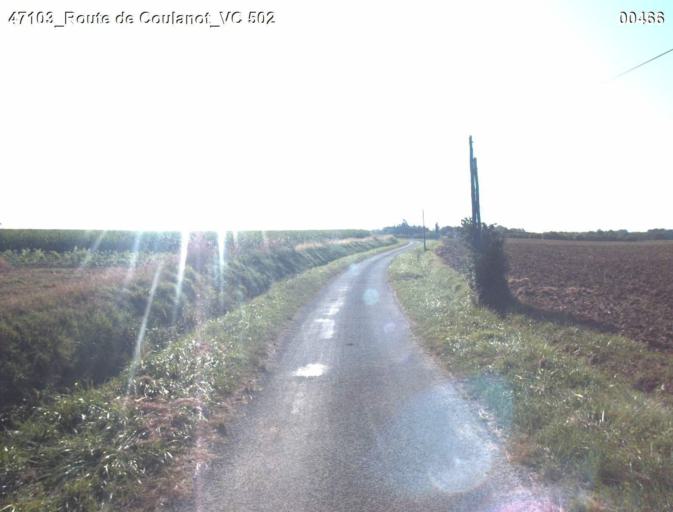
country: FR
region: Aquitaine
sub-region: Departement du Lot-et-Garonne
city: Nerac
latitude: 44.0748
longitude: 0.3347
